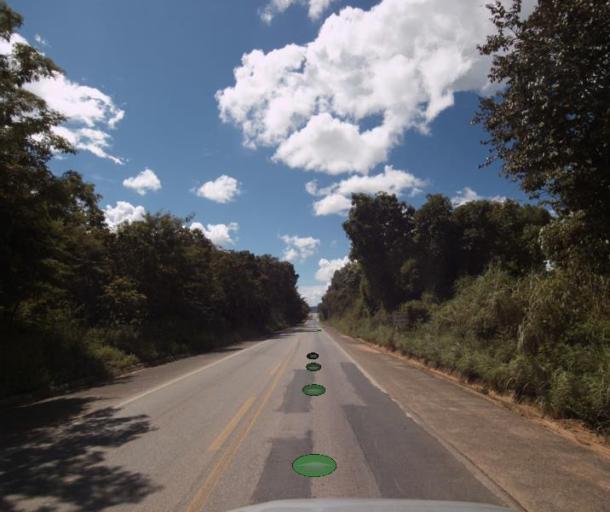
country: BR
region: Goias
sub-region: Porangatu
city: Porangatu
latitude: -13.7197
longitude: -49.0212
